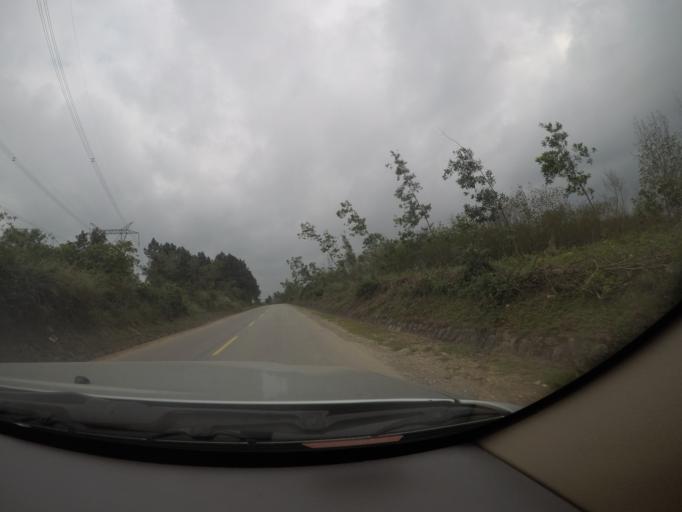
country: VN
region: Quang Binh
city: Kien Giang
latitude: 17.1734
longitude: 106.7385
